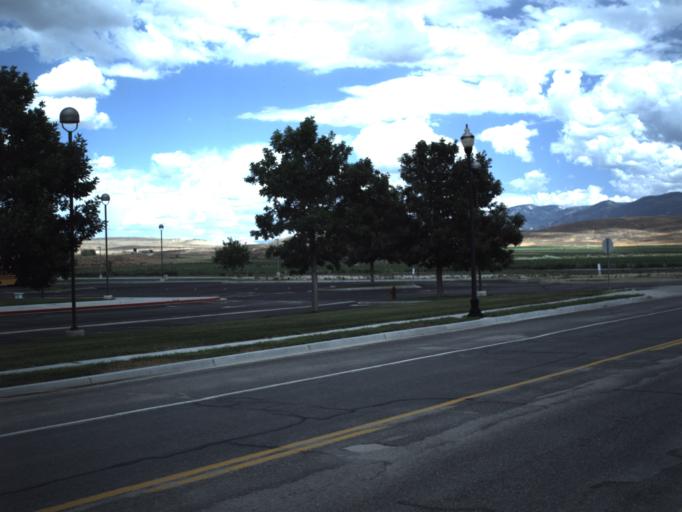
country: US
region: Utah
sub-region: Sanpete County
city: Gunnison
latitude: 39.1418
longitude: -111.8109
